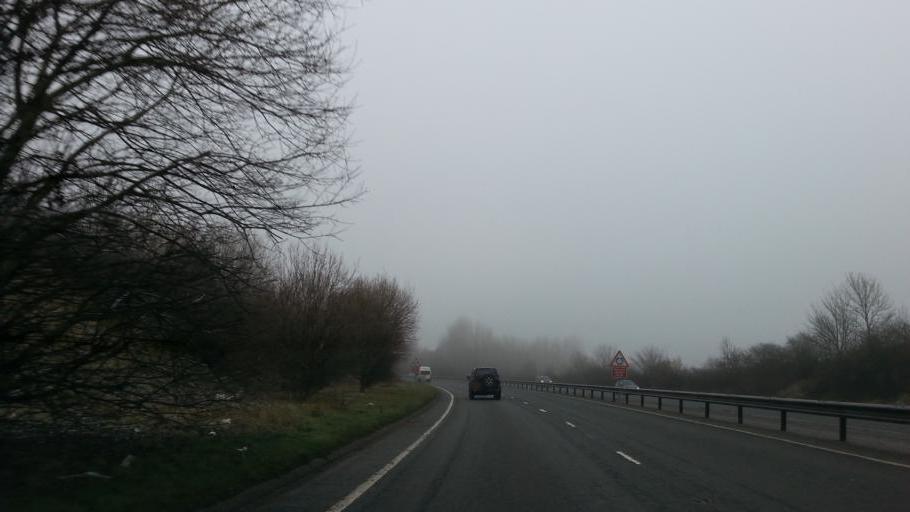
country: GB
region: England
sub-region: Cheshire East
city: Wilmslow
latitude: 53.3158
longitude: -2.2281
